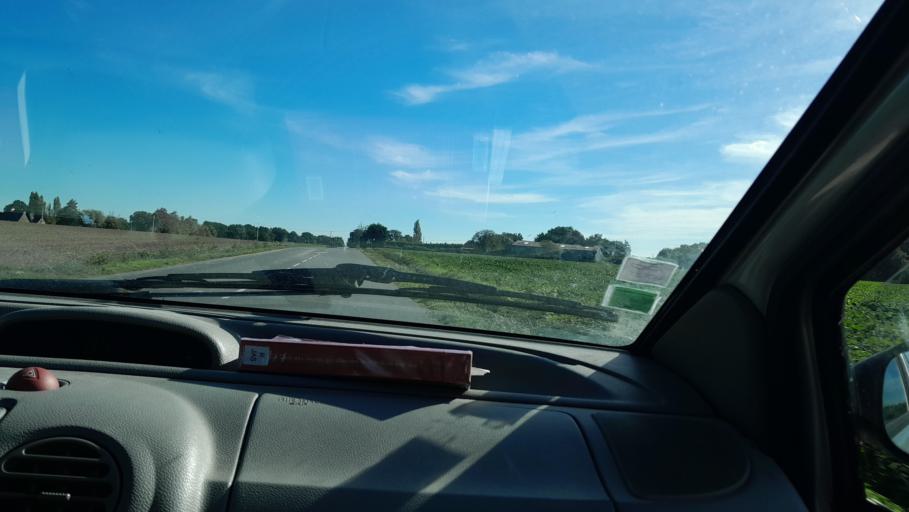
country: FR
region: Brittany
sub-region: Departement d'Ille-et-Vilaine
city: Argentre-du-Plessis
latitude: 48.0305
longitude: -1.1408
